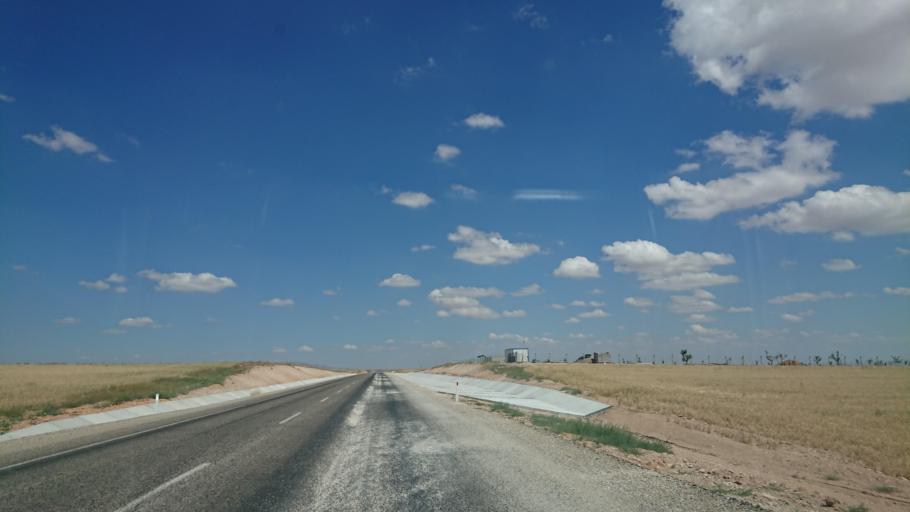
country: TR
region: Kirsehir
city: Kirsehir
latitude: 39.1236
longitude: 33.9950
